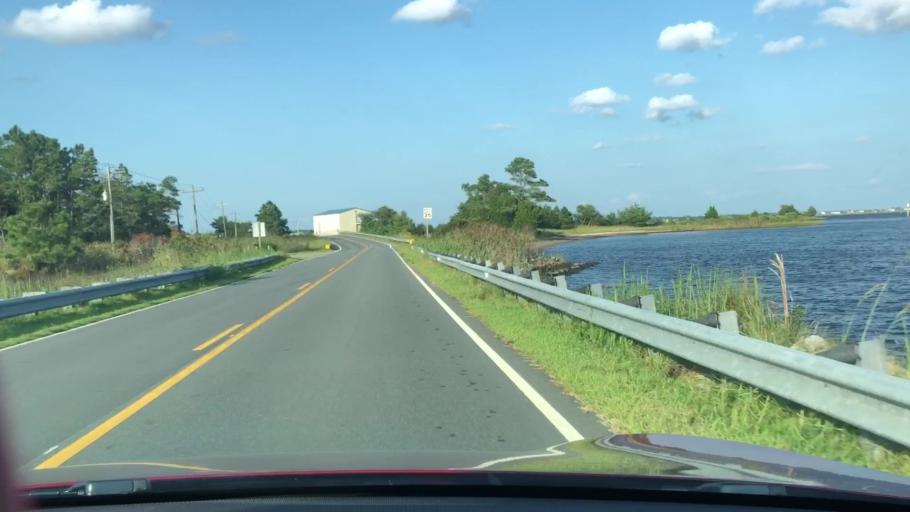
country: US
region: North Carolina
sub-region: Dare County
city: Wanchese
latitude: 35.6956
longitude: -75.7755
